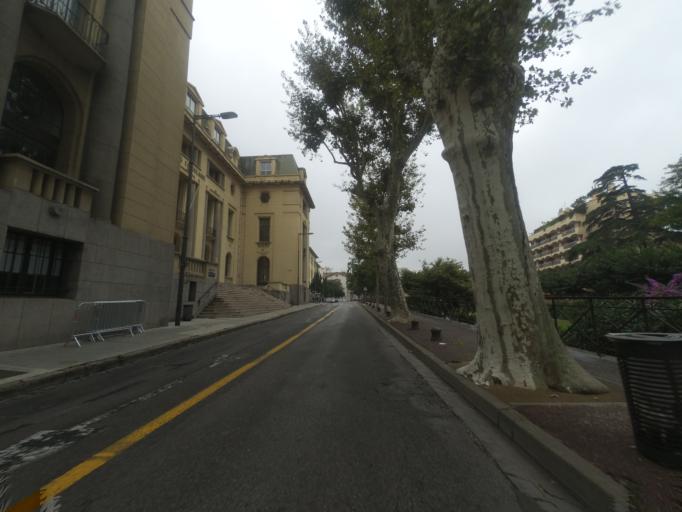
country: FR
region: Languedoc-Roussillon
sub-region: Departement des Pyrenees-Orientales
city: Perpignan
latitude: 42.6978
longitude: 2.8909
